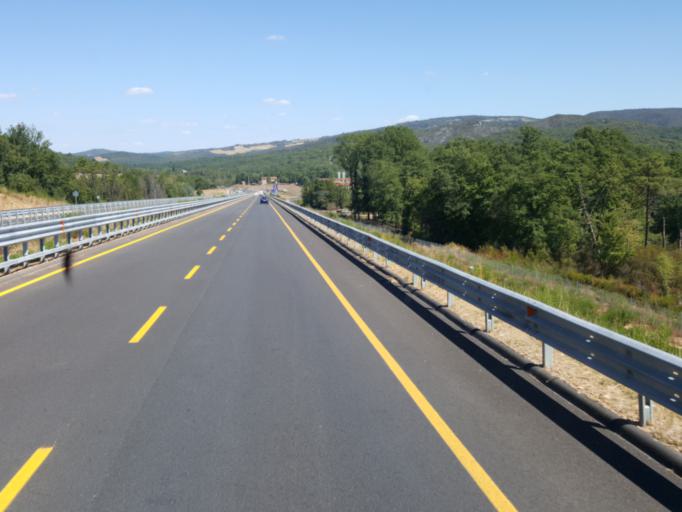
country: IT
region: Tuscany
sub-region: Provincia di Siena
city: Murlo
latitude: 43.1095
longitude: 11.2957
